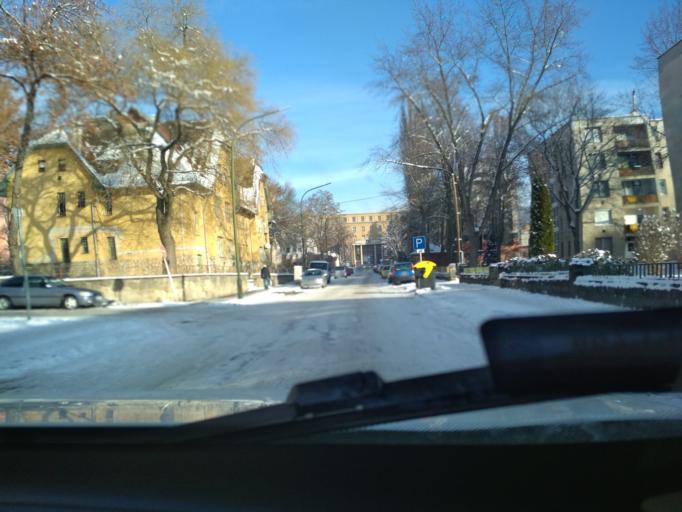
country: HU
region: Nograd
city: Salgotarjan
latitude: 48.1123
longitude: 19.8201
